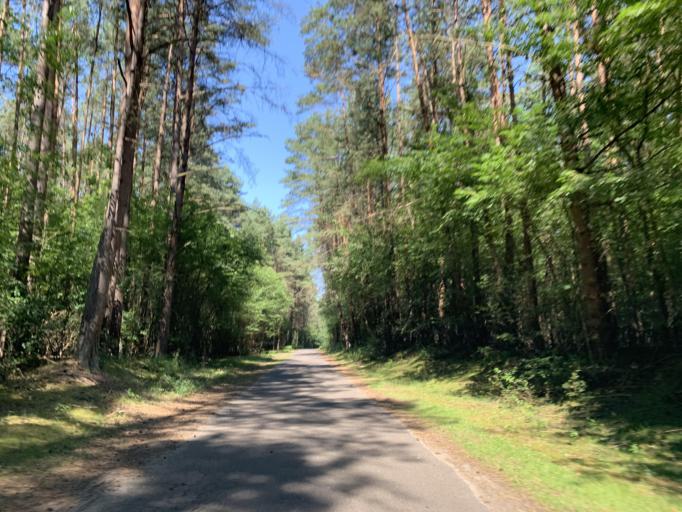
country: DE
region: Mecklenburg-Vorpommern
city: Carpin
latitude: 53.3120
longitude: 13.2970
